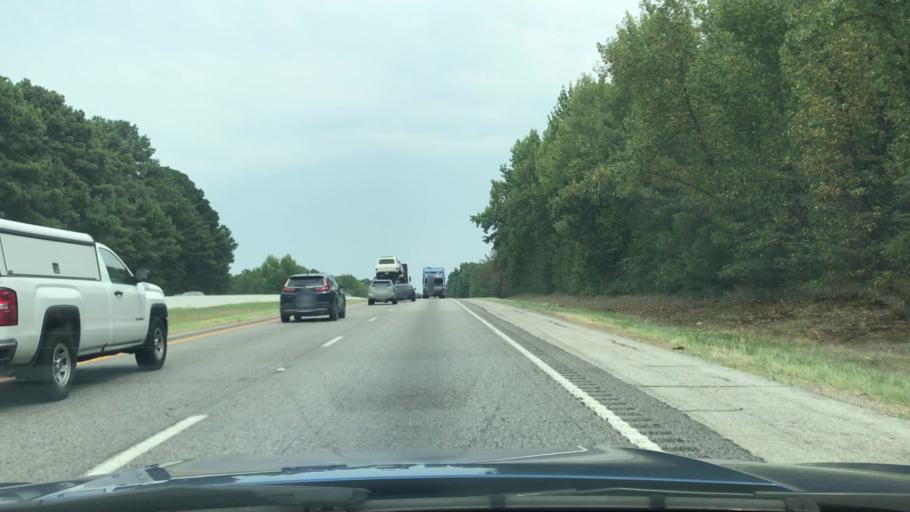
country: US
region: Texas
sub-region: Smith County
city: Lindale
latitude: 32.4642
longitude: -95.3312
